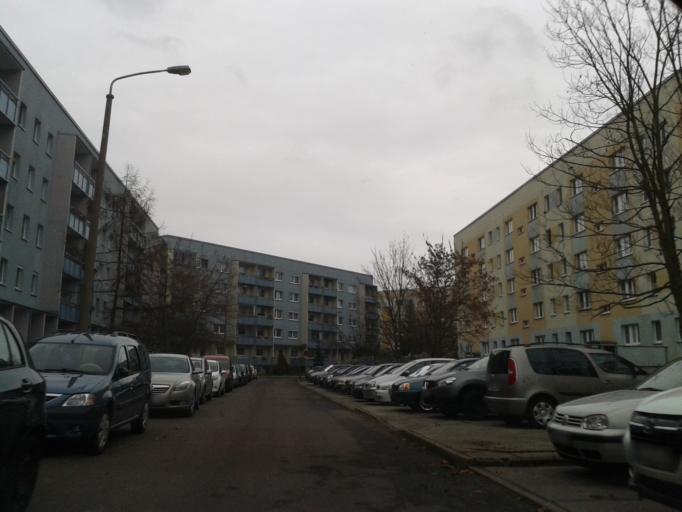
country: DE
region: Saxony-Anhalt
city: Halle Neustadt
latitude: 51.4504
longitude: 11.9554
